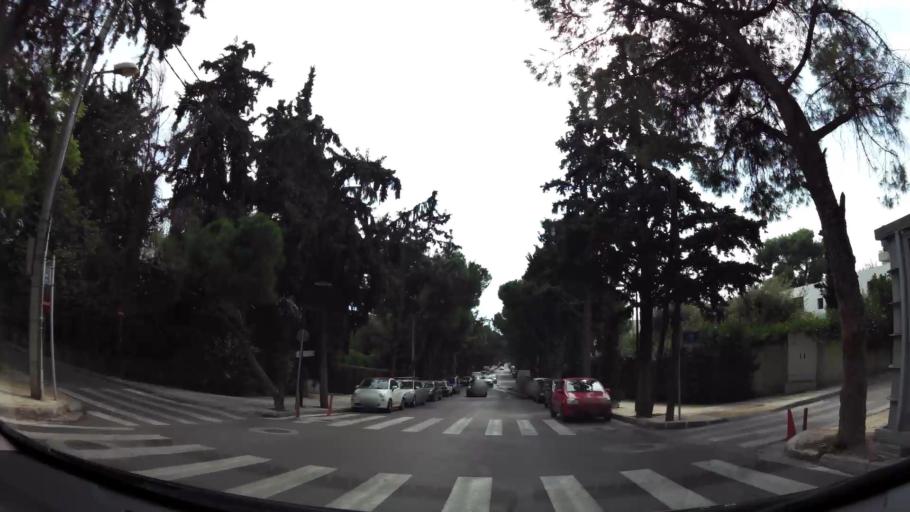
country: GR
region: Attica
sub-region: Nomarchia Athinas
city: Psychiko
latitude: 38.0170
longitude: 23.7706
